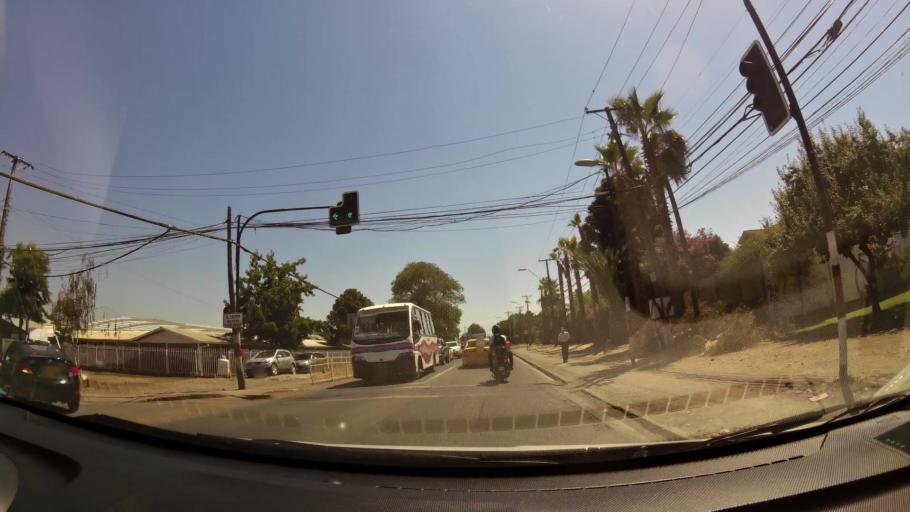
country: CL
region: Maule
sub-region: Provincia de Curico
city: Curico
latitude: -34.9669
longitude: -71.2299
